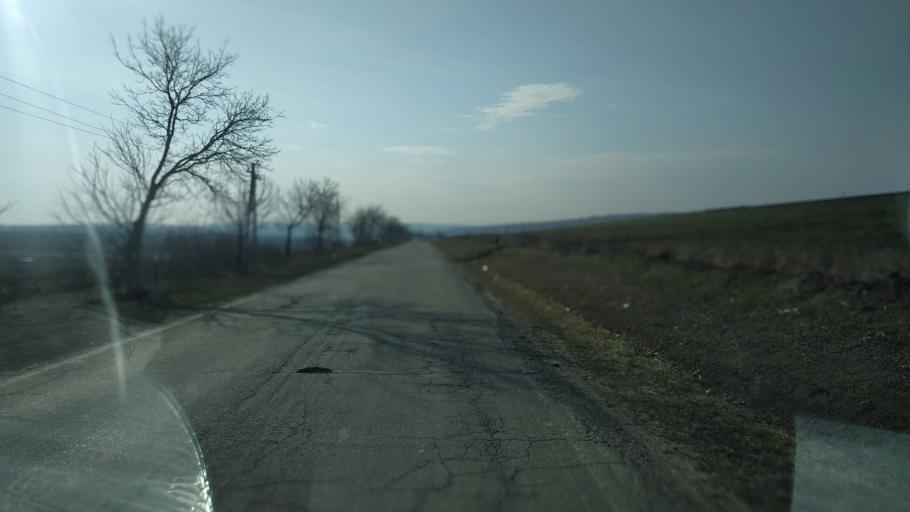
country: MD
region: Chisinau
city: Singera
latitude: 46.8516
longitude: 29.0227
